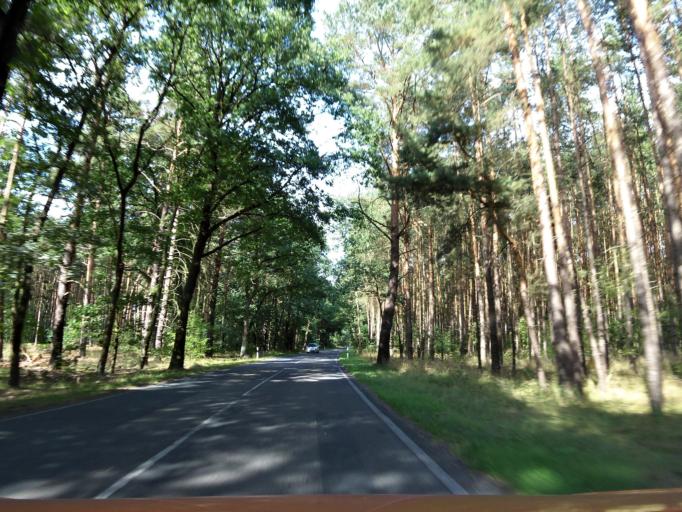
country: DE
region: Brandenburg
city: Michendorf
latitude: 52.2940
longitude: 13.1127
